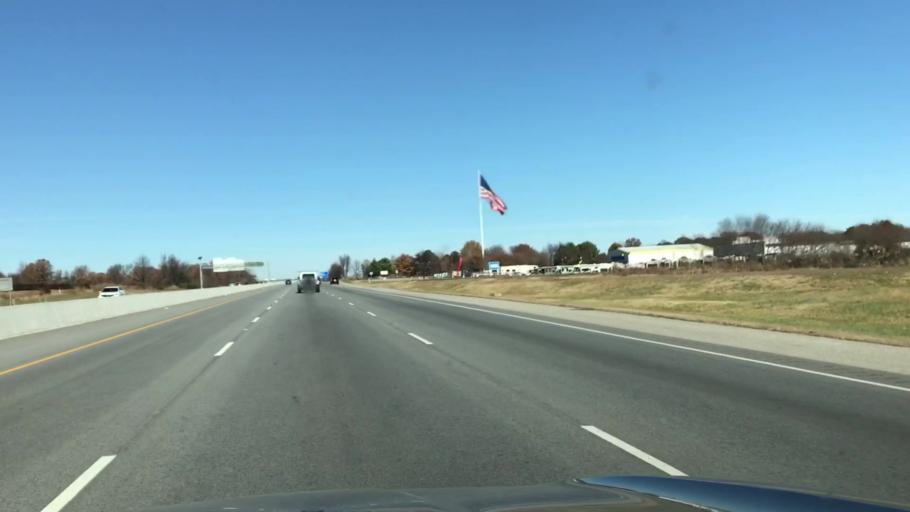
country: US
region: Arkansas
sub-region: Benton County
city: Lowell
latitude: 36.2568
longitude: -94.1502
